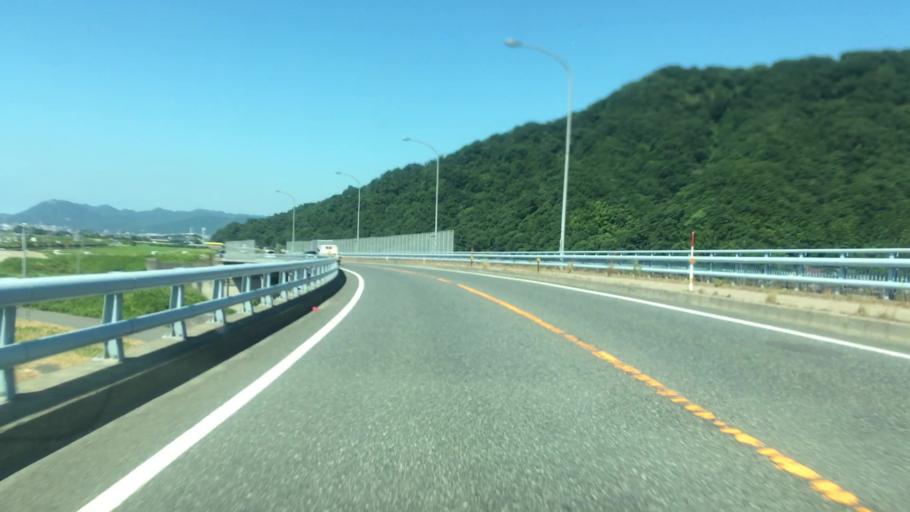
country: JP
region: Tottori
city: Tottori
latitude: 35.4395
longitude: 134.2089
